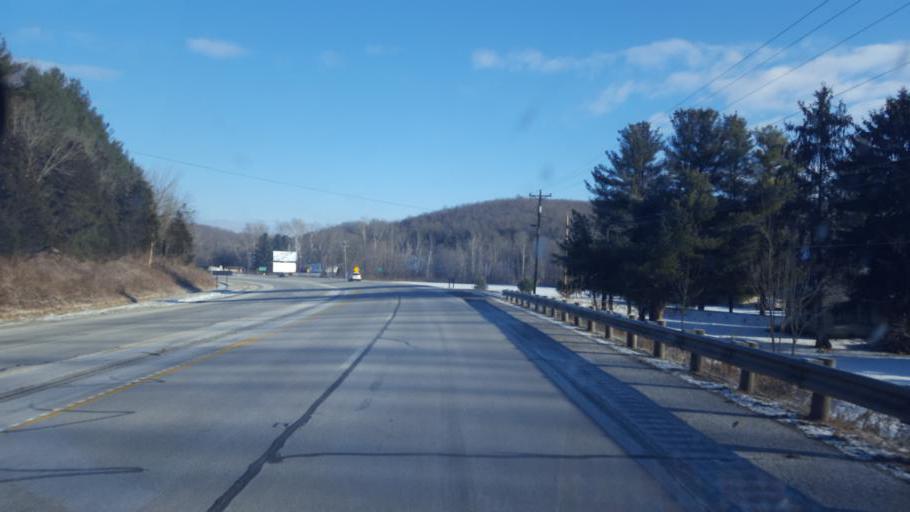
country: US
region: Ohio
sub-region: Pike County
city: Waverly
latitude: 39.1779
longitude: -82.9731
